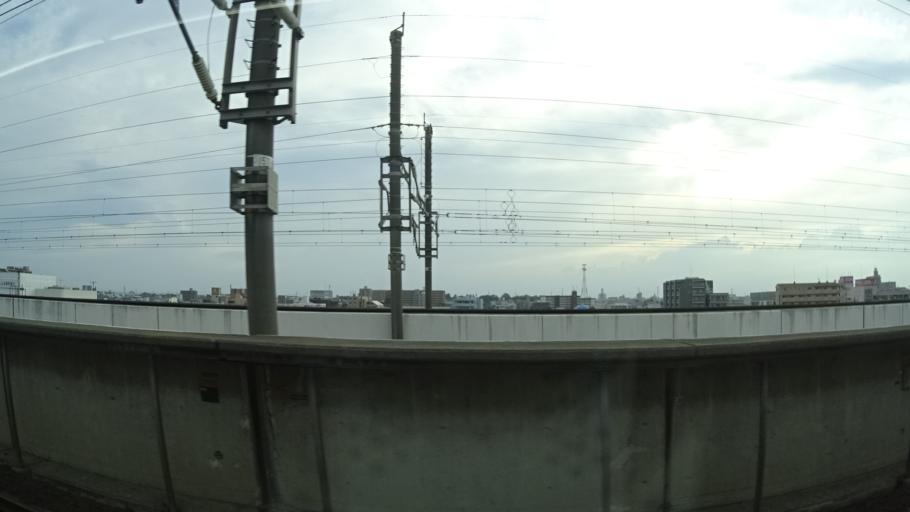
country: JP
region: Saitama
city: Yono
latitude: 35.9210
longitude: 139.6177
